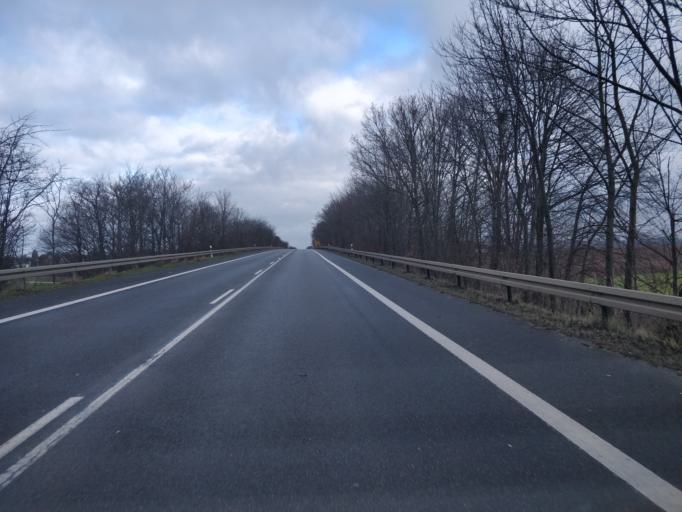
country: DE
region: North Rhine-Westphalia
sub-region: Regierungsbezirk Koln
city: Euskirchen
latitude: 50.6539
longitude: 6.8430
